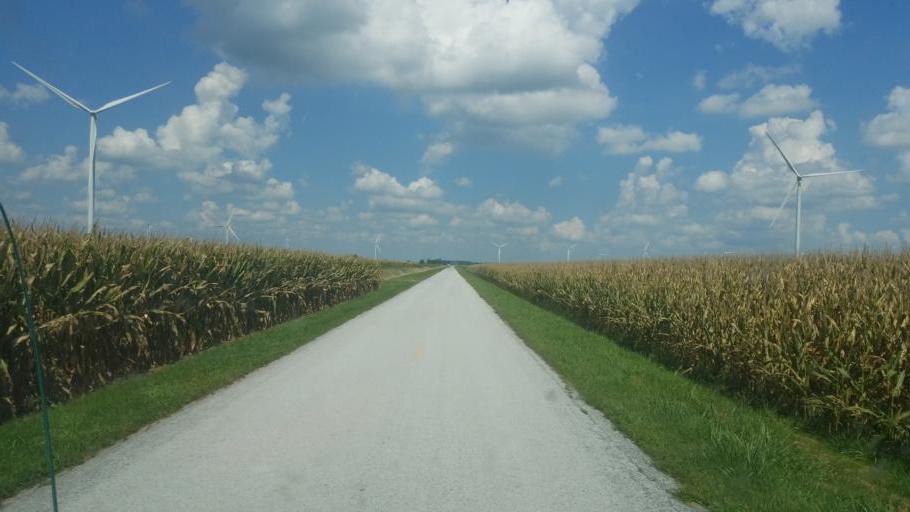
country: US
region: Ohio
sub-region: Hardin County
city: Ada
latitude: 40.7660
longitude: -83.7287
